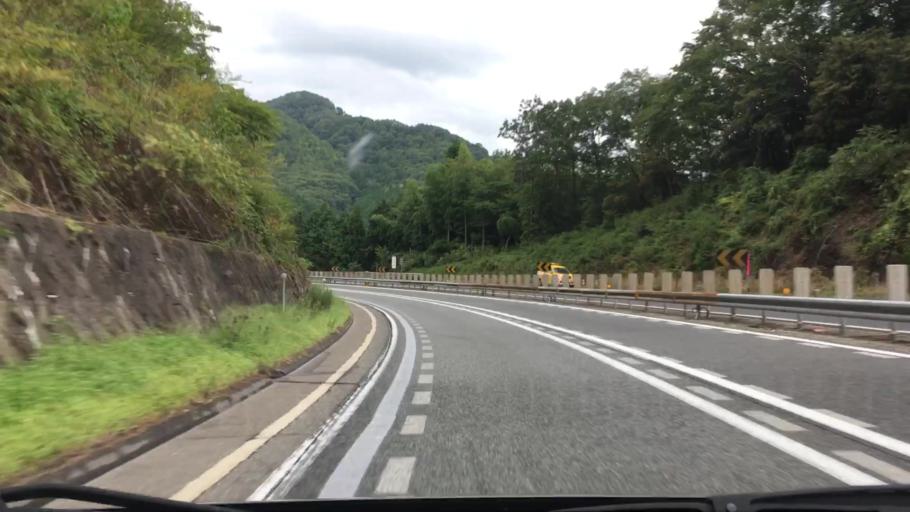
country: JP
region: Okayama
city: Niimi
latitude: 35.0289
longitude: 133.5262
